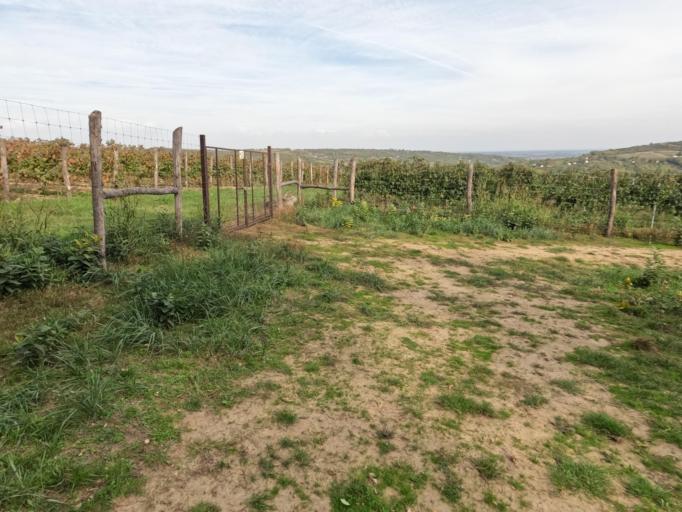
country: HU
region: Tolna
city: Szentgalpuszta
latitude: 46.3301
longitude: 18.6528
